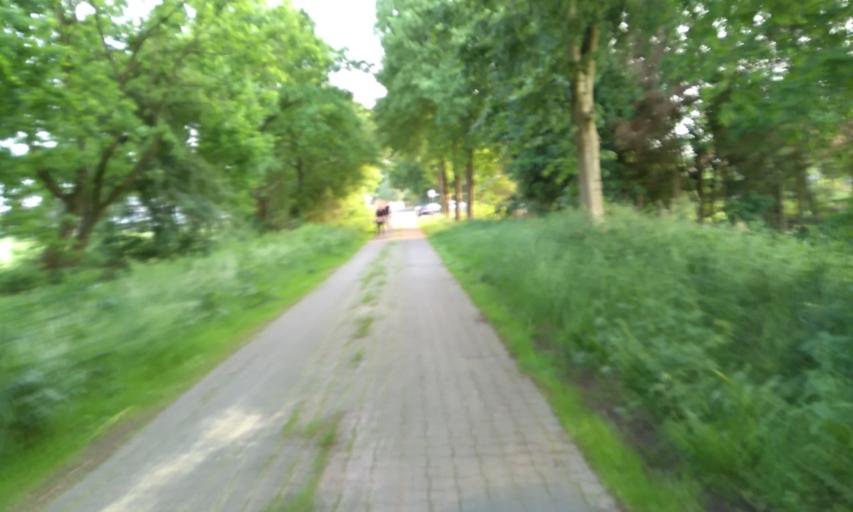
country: DE
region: Lower Saxony
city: Deinste
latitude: 53.5258
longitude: 9.4882
